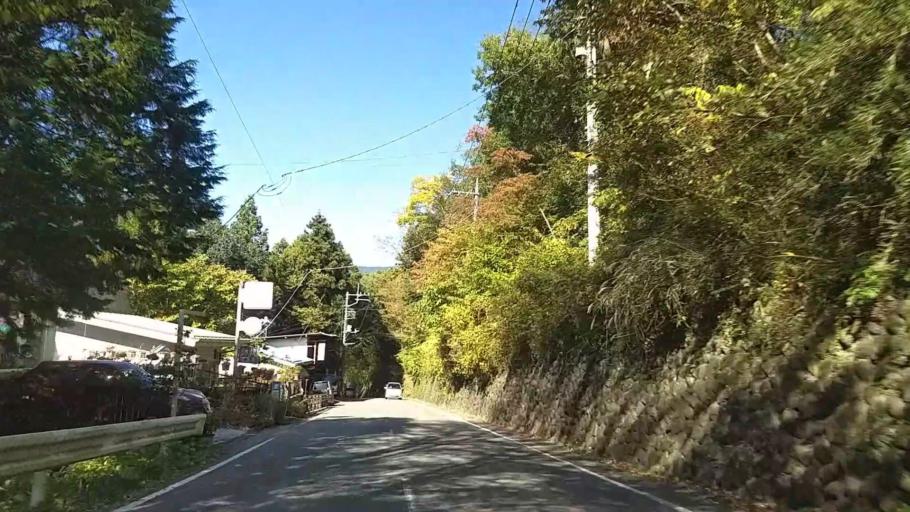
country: JP
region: Yamanashi
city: Uenohara
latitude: 35.6415
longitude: 139.1025
